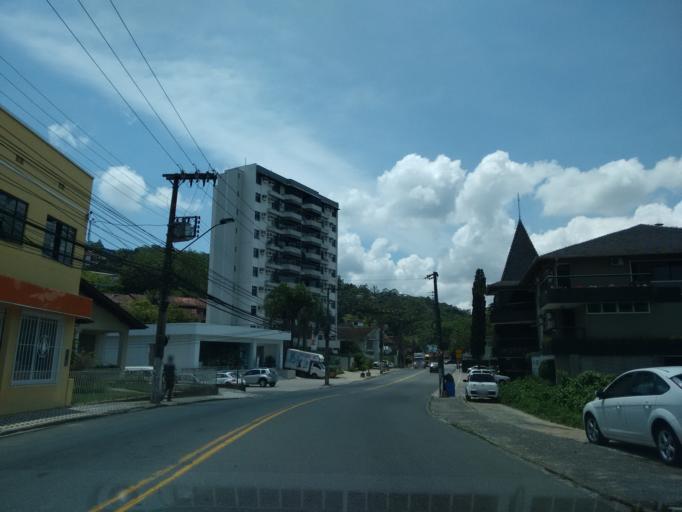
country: BR
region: Santa Catarina
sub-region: Blumenau
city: Blumenau
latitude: -26.9139
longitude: -49.0600
